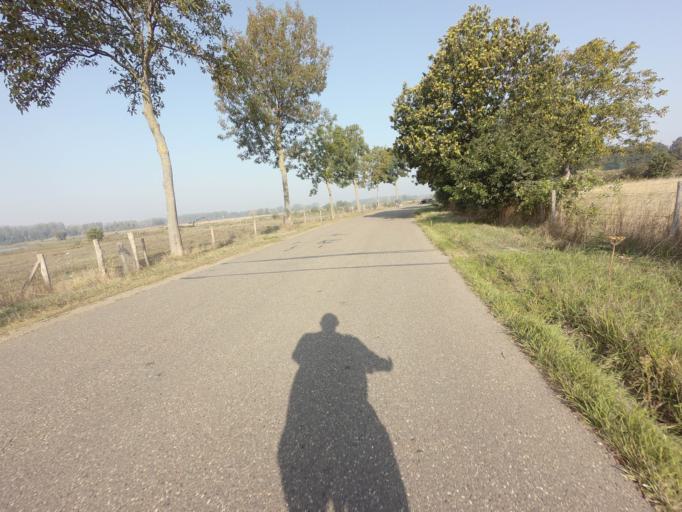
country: NL
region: Limburg
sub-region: Gemeente Roermond
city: Leeuwen
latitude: 51.2134
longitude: 5.9914
